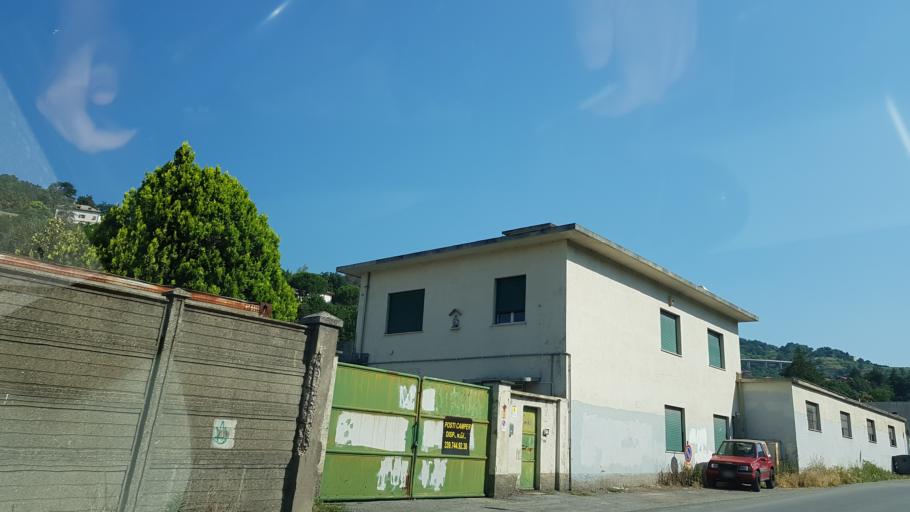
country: IT
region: Liguria
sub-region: Provincia di Genova
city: Pedemonte
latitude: 44.5037
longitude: 8.9278
